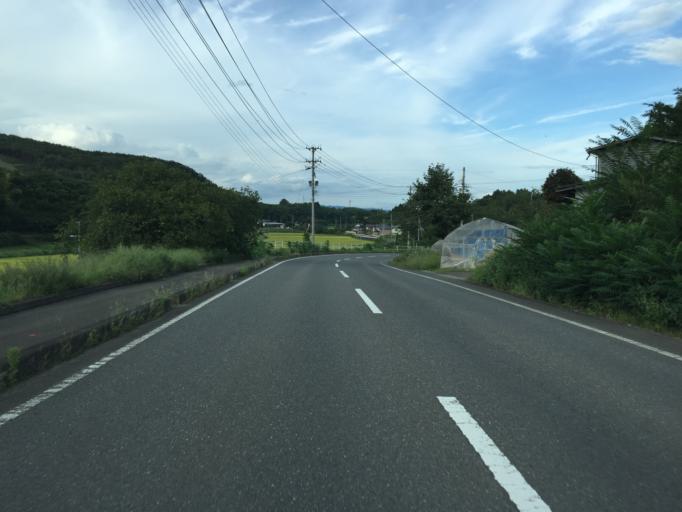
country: JP
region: Fukushima
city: Hobaramachi
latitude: 37.7913
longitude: 140.5353
